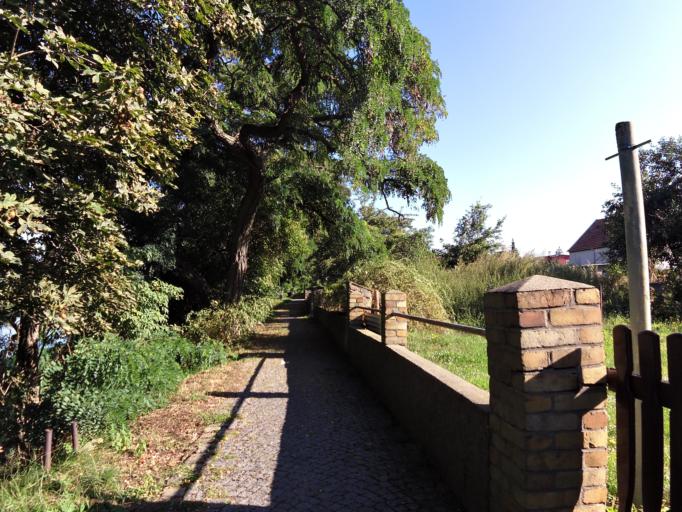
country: DE
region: Saxony
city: Nunchritz
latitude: 51.2667
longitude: 13.4050
